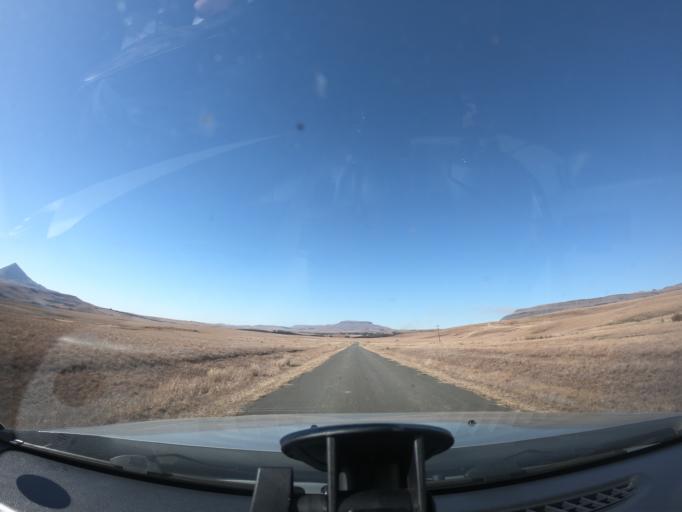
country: ZA
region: KwaZulu-Natal
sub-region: uMgungundlovu District Municipality
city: Impendle
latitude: -29.3853
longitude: 29.7195
